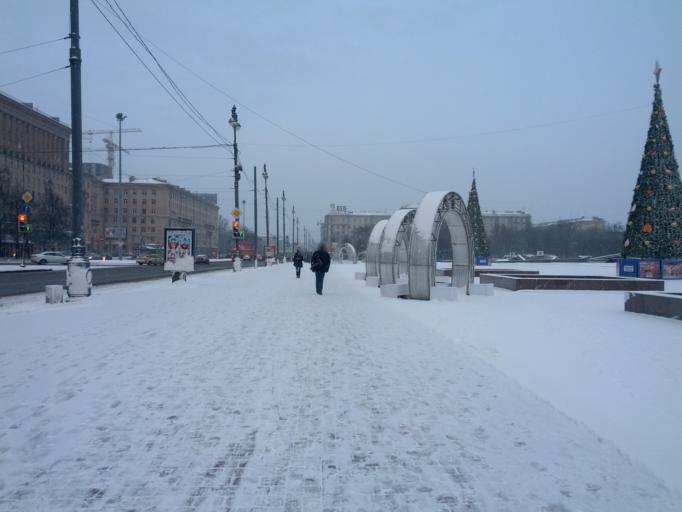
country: RU
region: St.-Petersburg
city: Kupchino
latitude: 59.8515
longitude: 30.3219
